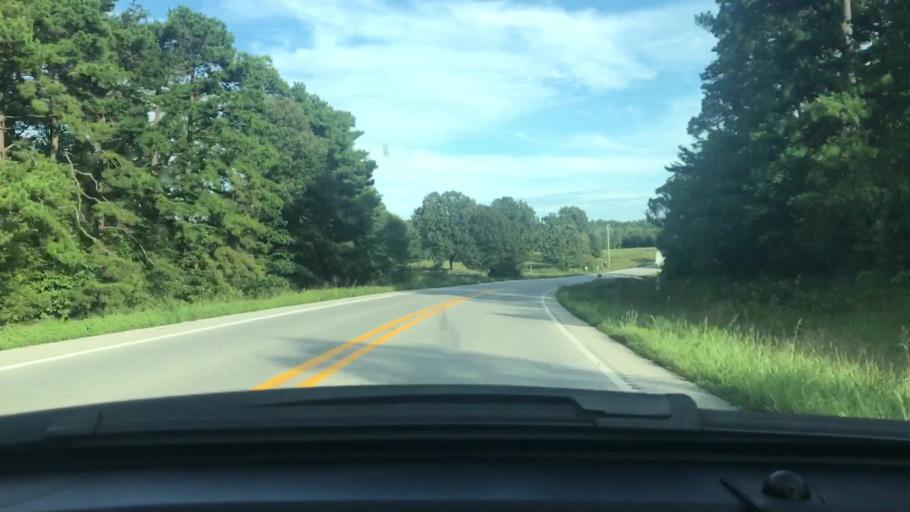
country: US
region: Arkansas
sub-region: Sharp County
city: Cherokee Village
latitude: 36.2761
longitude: -91.3102
